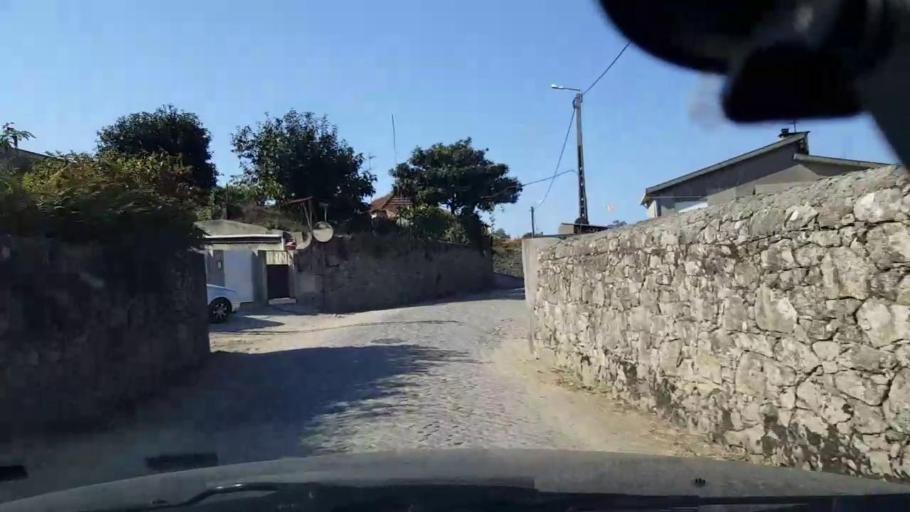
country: PT
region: Porto
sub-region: Vila do Conde
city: Arvore
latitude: 41.3616
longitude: -8.6964
